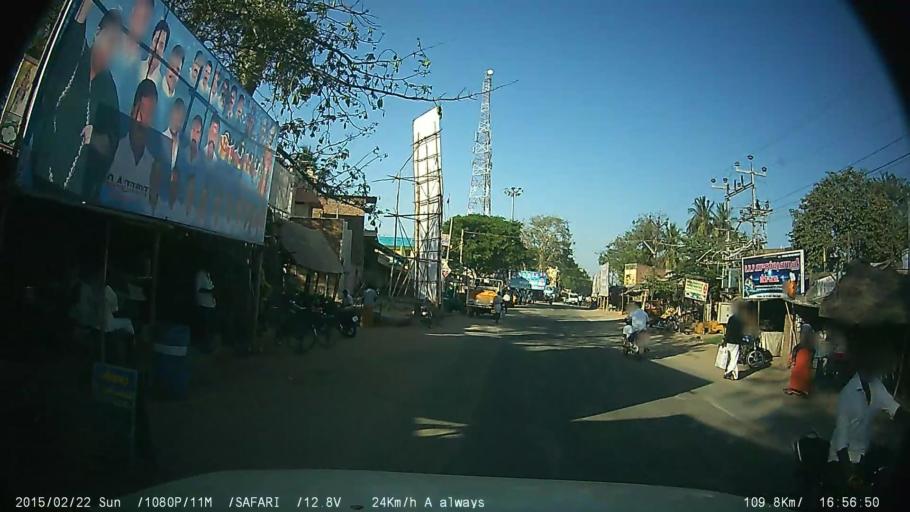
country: IN
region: Tamil Nadu
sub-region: Theni
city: Gudalur
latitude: 9.6811
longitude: 77.2447
